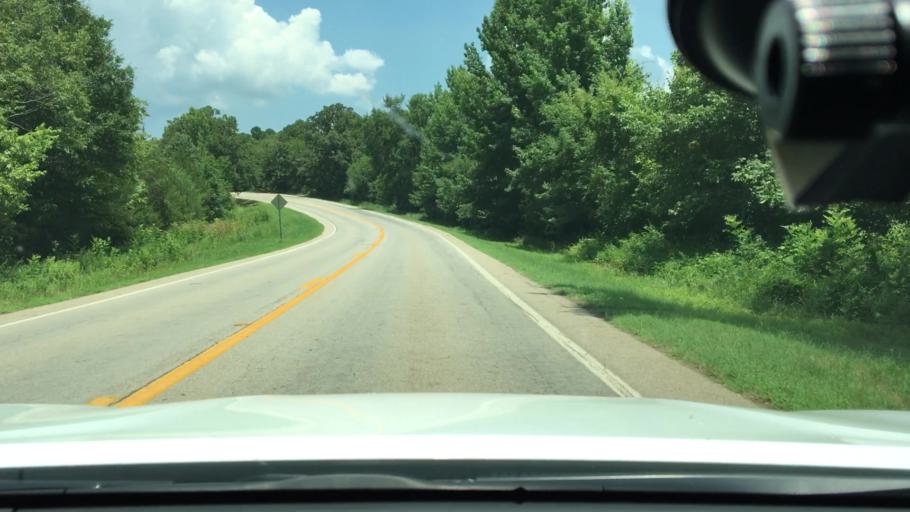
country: US
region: Arkansas
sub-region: Logan County
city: Booneville
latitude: 35.2072
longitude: -93.9244
